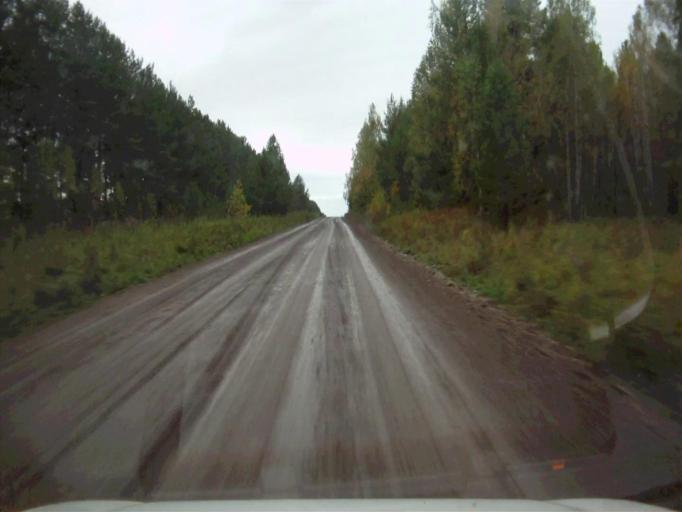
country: RU
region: Chelyabinsk
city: Nyazepetrovsk
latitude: 56.1420
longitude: 59.2906
